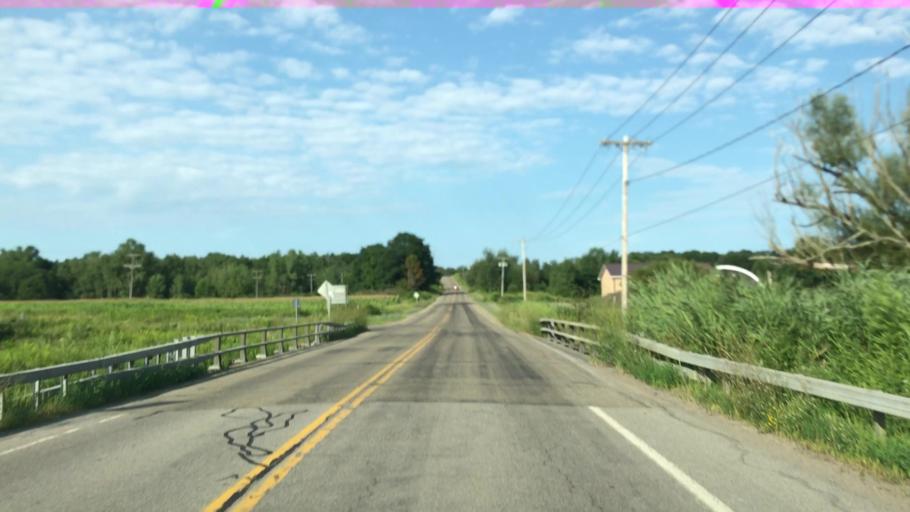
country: US
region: New York
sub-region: Chautauqua County
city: Brocton
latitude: 42.3145
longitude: -79.3640
